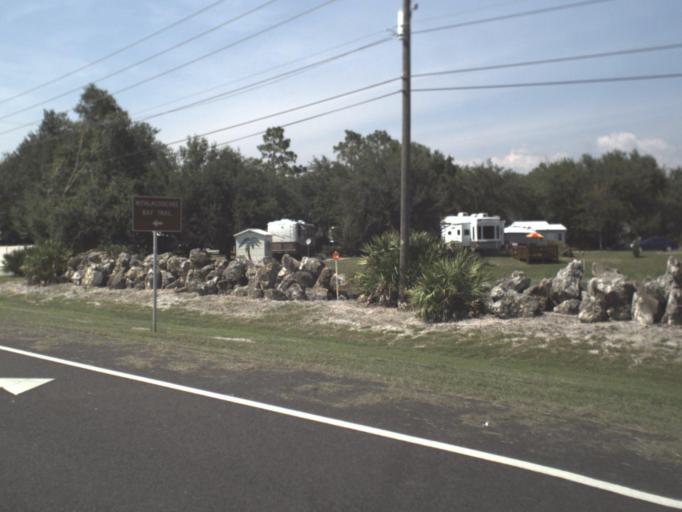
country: US
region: Florida
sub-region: Levy County
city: Inglis
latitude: 29.0065
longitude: -82.6592
